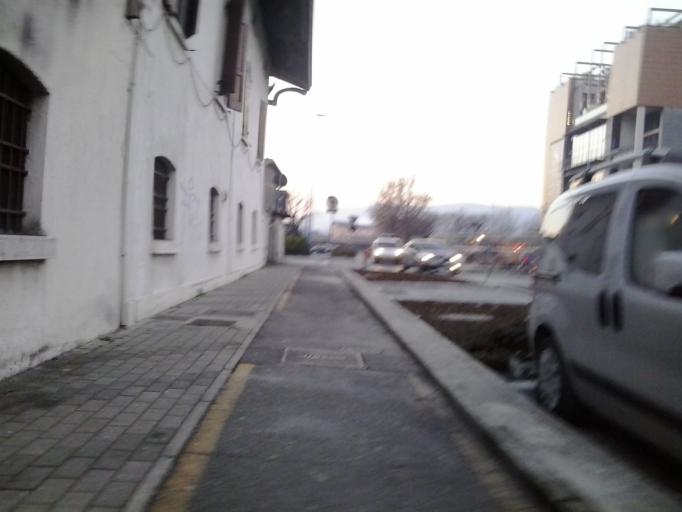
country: IT
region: Lombardy
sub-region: Provincia di Brescia
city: Collebeato
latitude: 45.5640
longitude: 10.2302
